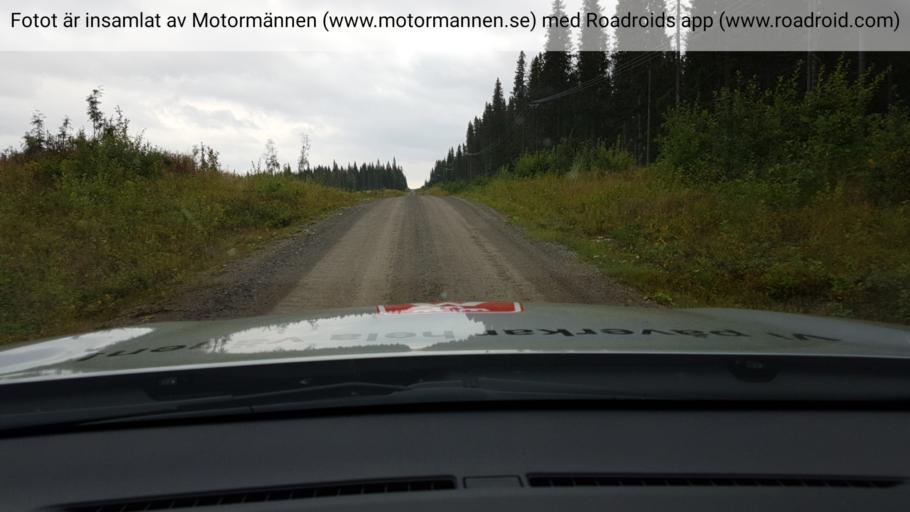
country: SE
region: Jaemtland
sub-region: Stroemsunds Kommun
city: Stroemsund
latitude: 63.7847
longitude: 15.3039
